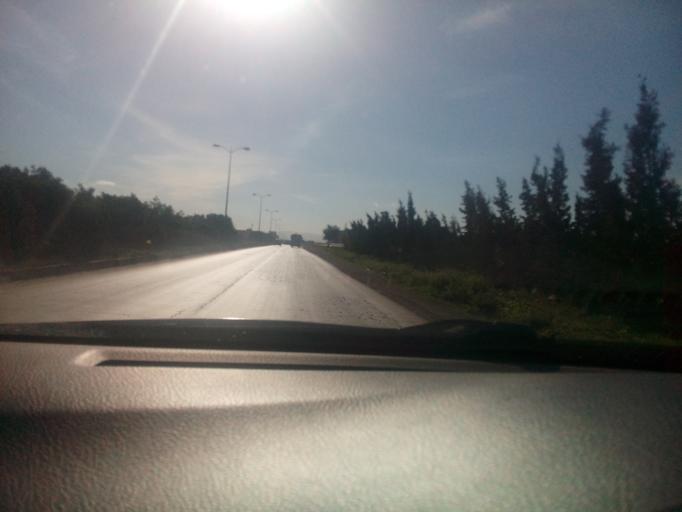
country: DZ
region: Oran
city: Sidi ech Chahmi
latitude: 35.6630
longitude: -0.5674
